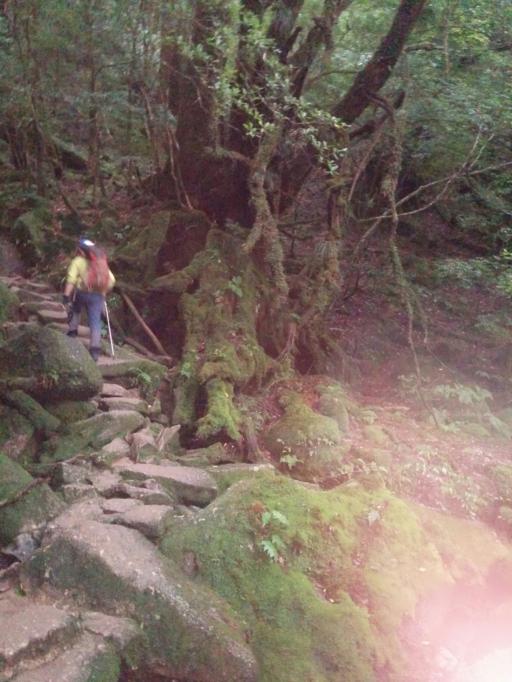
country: JP
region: Kagoshima
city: Nishinoomote
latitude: 30.3684
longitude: 130.5700
